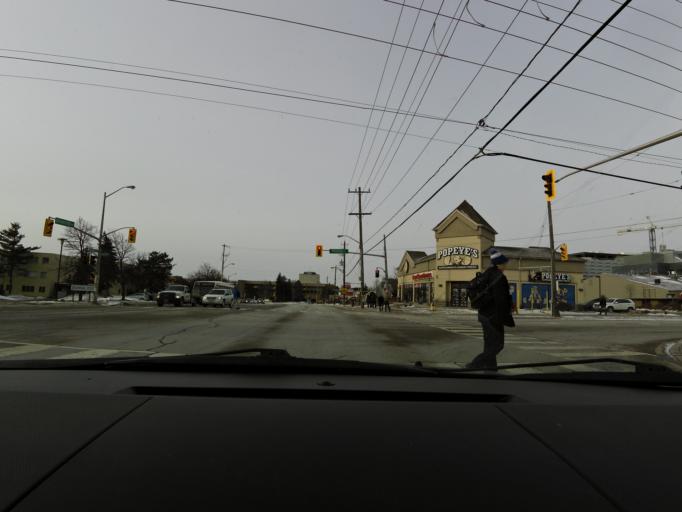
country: CA
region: Ontario
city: Waterloo
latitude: 43.4722
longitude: -80.5362
